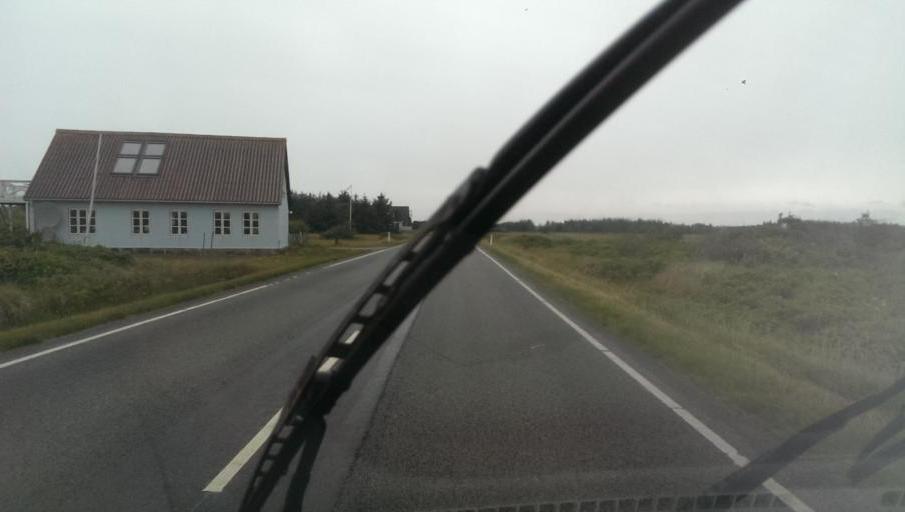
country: DK
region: Central Jutland
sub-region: Ringkobing-Skjern Kommune
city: Hvide Sande
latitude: 55.9324
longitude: 8.1603
